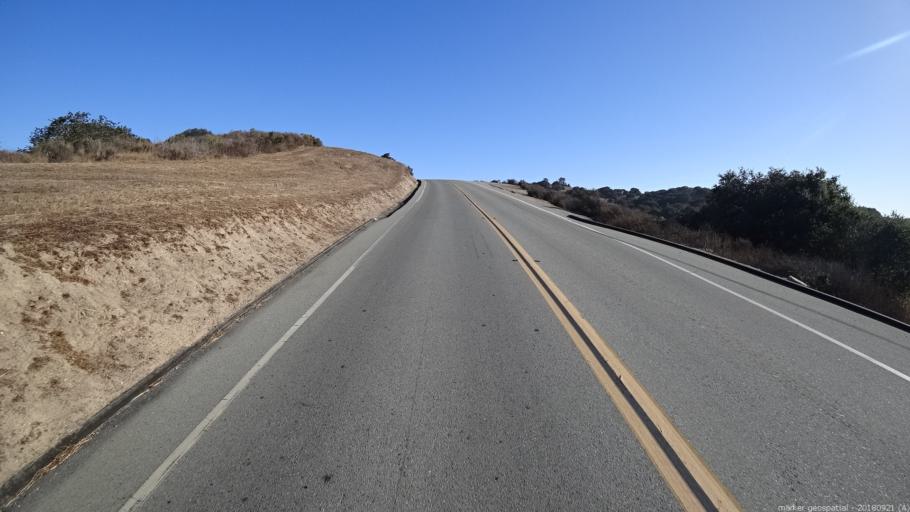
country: US
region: California
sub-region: Monterey County
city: Carmel Valley Village
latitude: 36.5733
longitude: -121.7619
